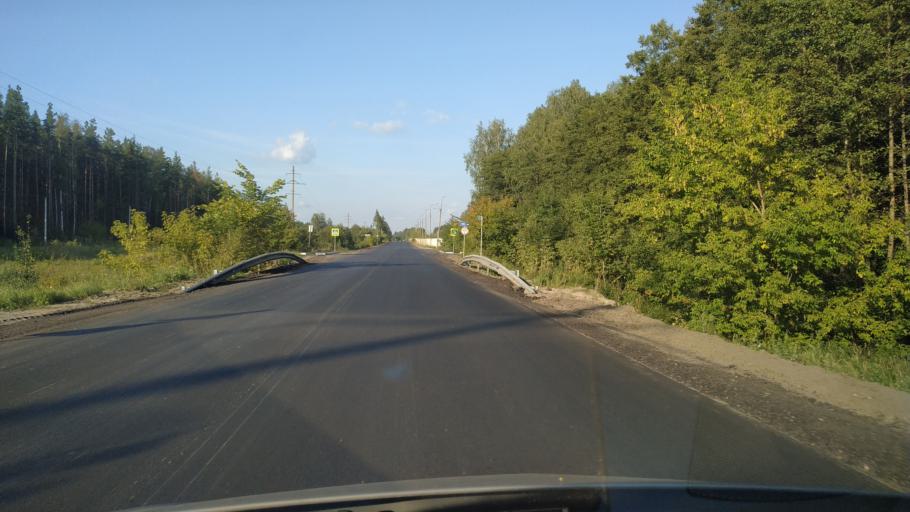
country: RU
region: Moskovskaya
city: Kerva
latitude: 55.5735
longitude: 39.6784
